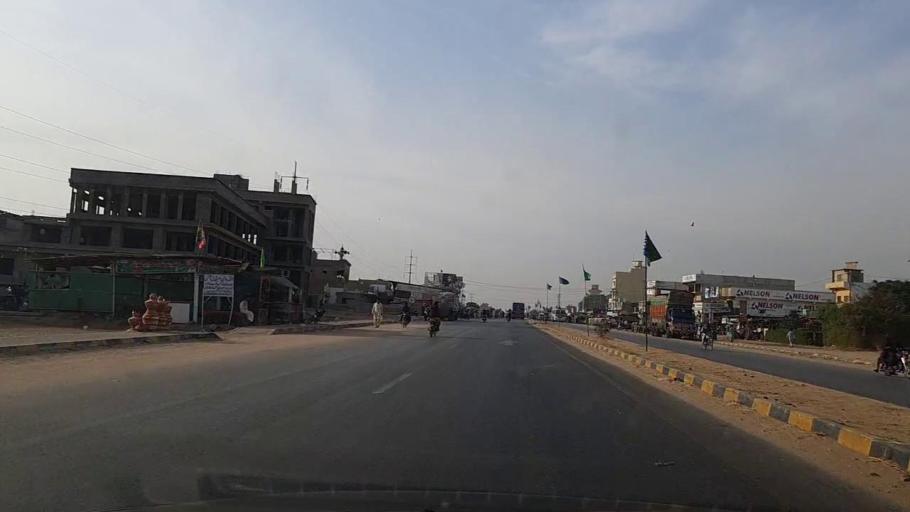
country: PK
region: Sindh
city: Gharo
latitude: 24.7900
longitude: 67.5263
